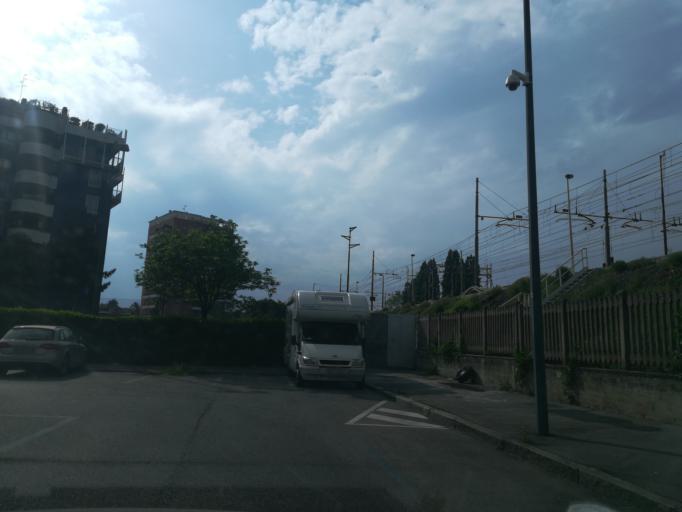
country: IT
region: Lombardy
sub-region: Citta metropolitana di Milano
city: Bresso
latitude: 45.5041
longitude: 9.1927
